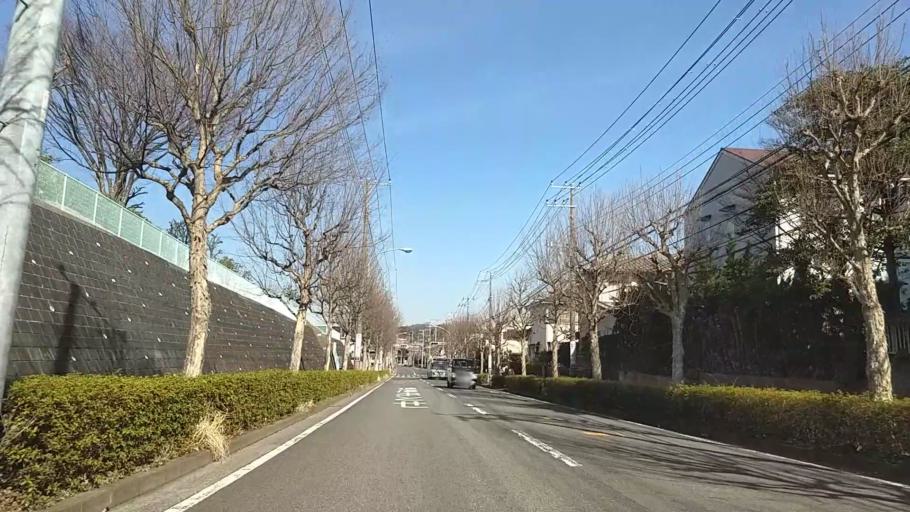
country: JP
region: Kanagawa
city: Kamakura
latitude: 35.3778
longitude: 139.5849
